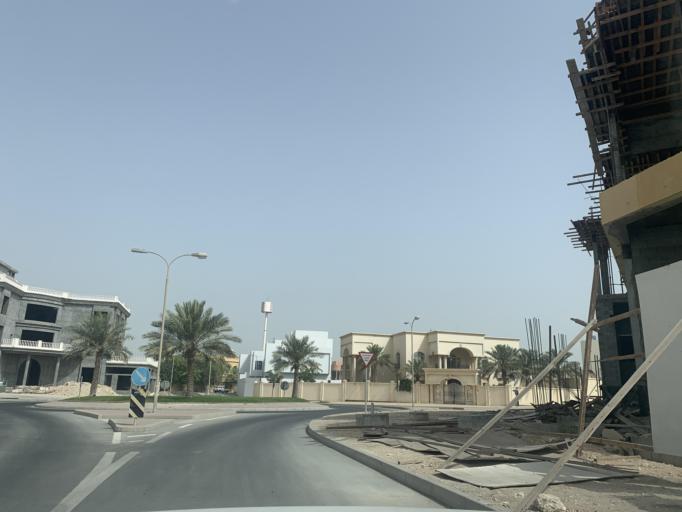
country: BH
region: Central Governorate
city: Madinat Hamad
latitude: 26.1436
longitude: 50.5153
